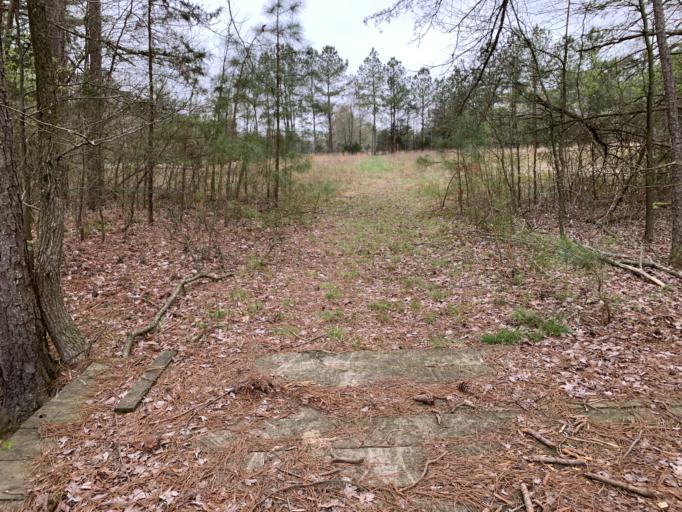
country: US
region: Delaware
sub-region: Kent County
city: Felton
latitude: 39.0355
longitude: -75.6432
